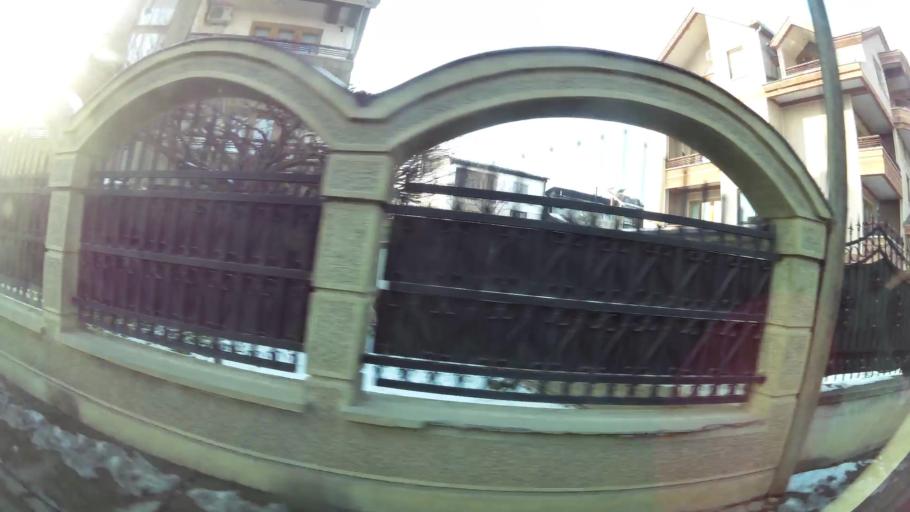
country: MK
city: Creshevo
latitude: 42.0137
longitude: 21.5095
